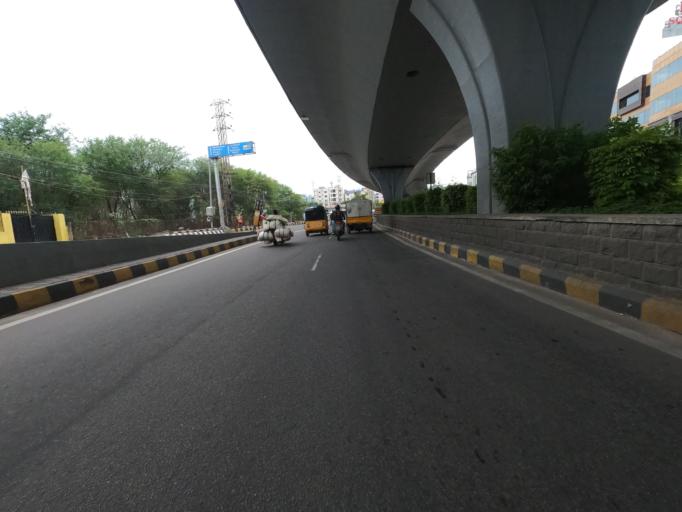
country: IN
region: Telangana
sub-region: Hyderabad
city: Hyderabad
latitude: 17.3518
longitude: 78.4178
